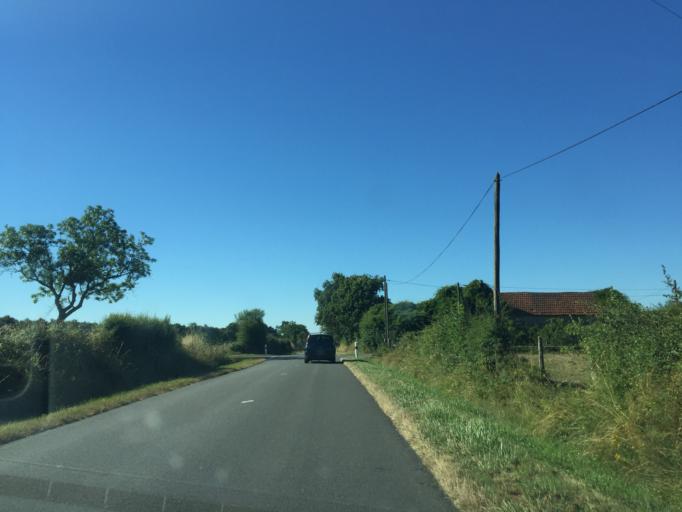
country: FR
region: Auvergne
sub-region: Departement de l'Allier
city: Dompierre-sur-Besbre
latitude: 46.5171
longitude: 3.6215
